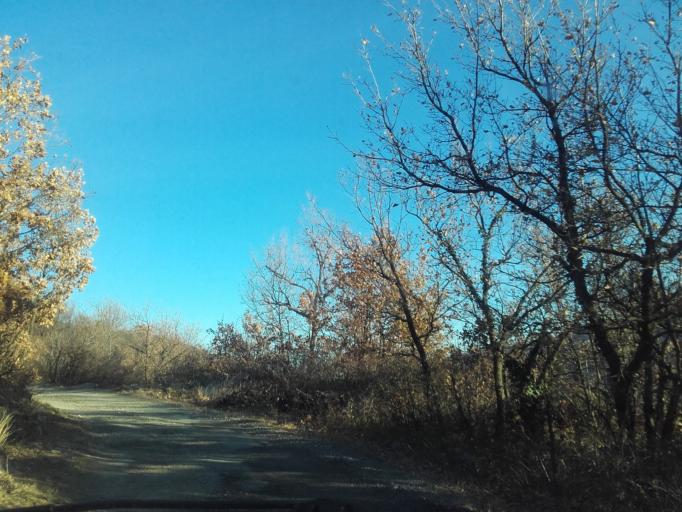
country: IT
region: Piedmont
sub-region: Provincia di Torino
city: Bussoleno
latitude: 45.1496
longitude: 7.1352
